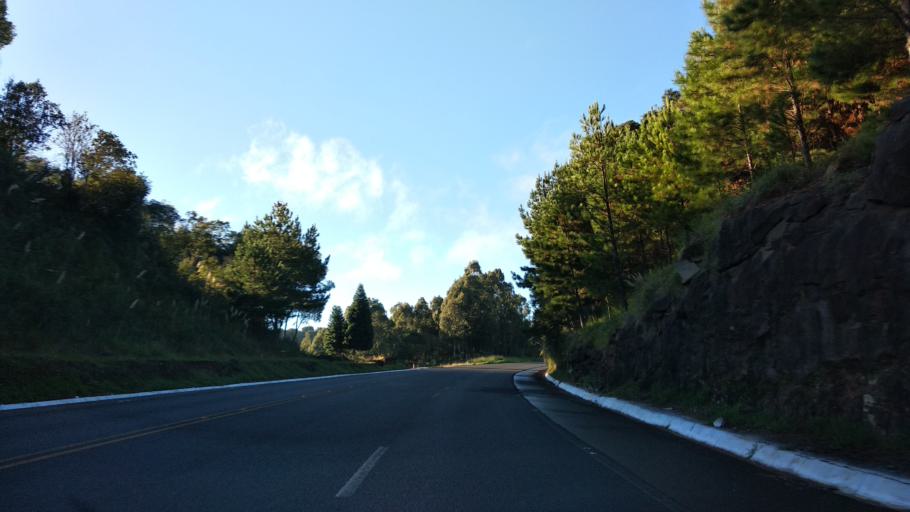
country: BR
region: Santa Catarina
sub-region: Curitibanos
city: Curitibanos
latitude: -27.6073
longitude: -50.7191
